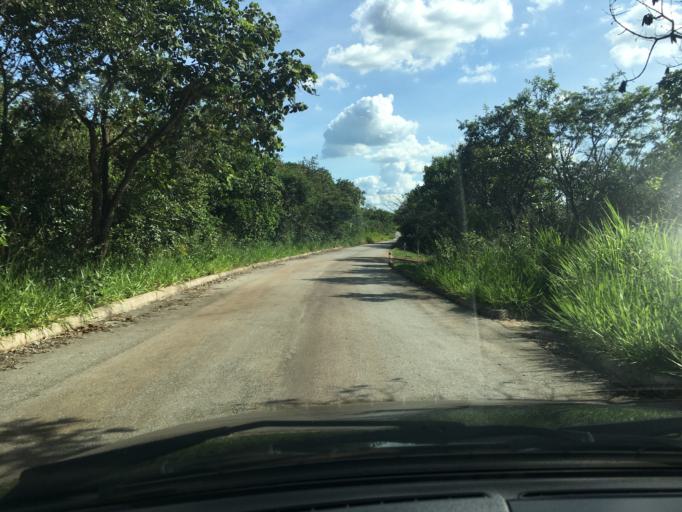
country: BR
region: Minas Gerais
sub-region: Ibirite
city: Ibirite
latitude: -20.1266
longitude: -44.0686
